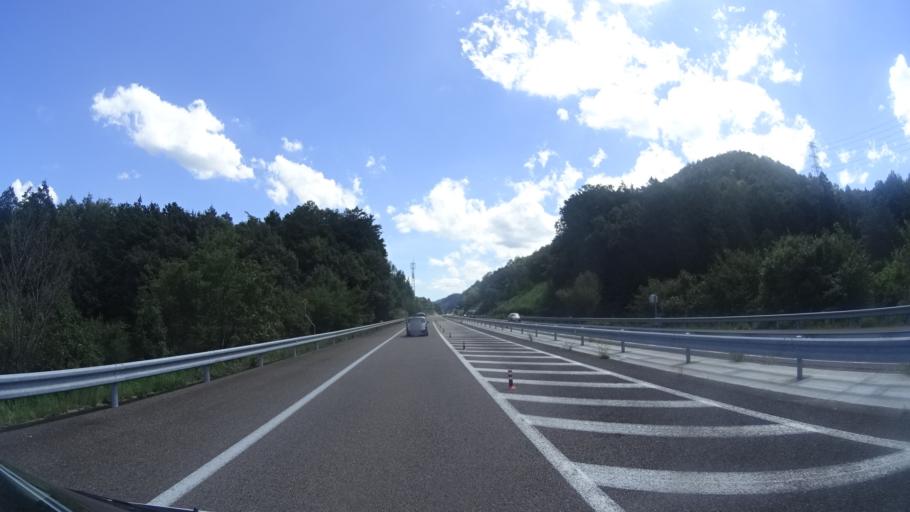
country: JP
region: Gifu
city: Mino
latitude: 35.5156
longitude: 136.9469
